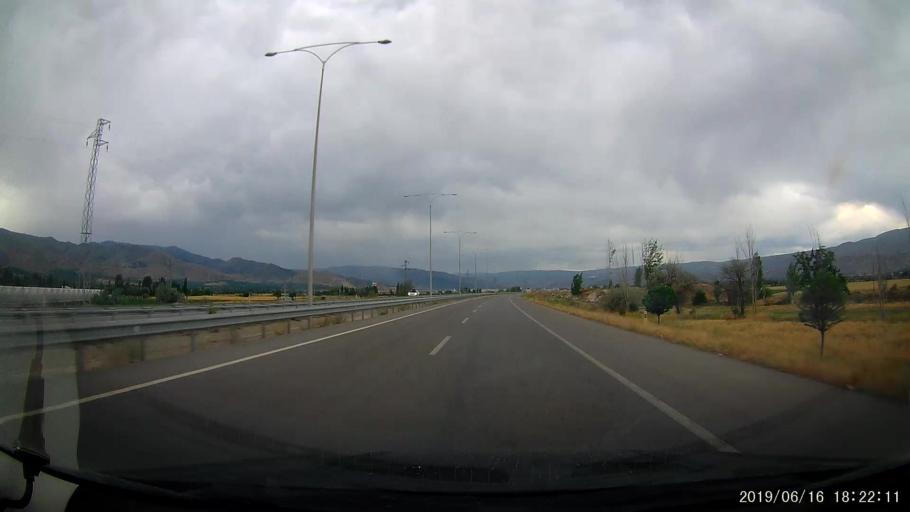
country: TR
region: Erzincan
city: Erzincan
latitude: 39.7287
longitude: 39.4285
